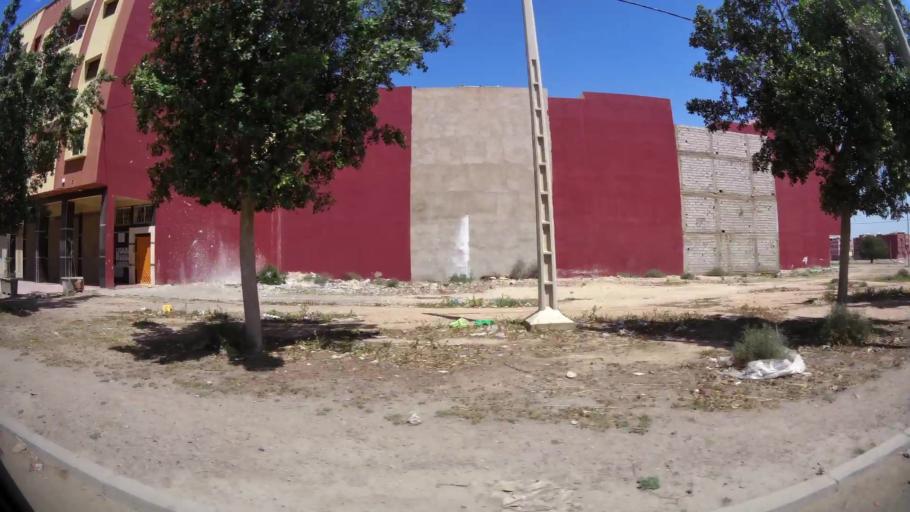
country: MA
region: Souss-Massa-Draa
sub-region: Inezgane-Ait Mellou
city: Inezgane
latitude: 30.3212
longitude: -9.5005
